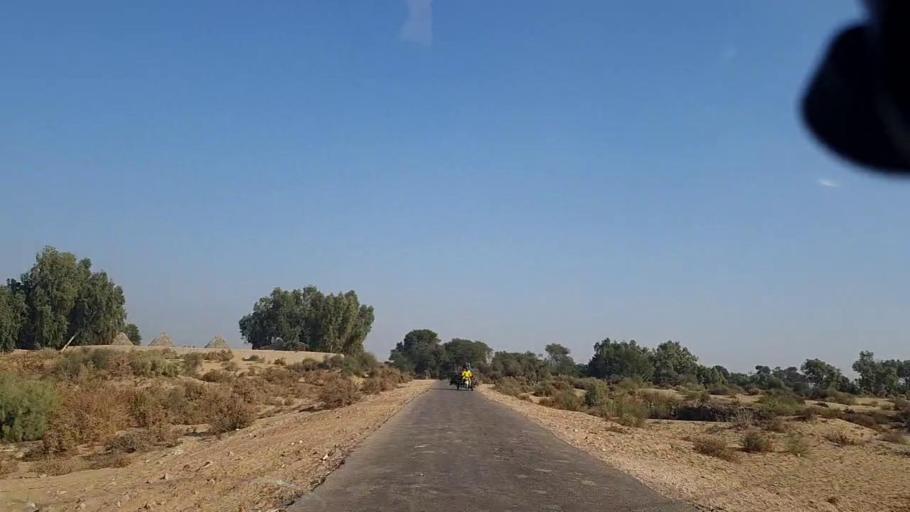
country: PK
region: Sindh
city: Khanpur
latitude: 27.6860
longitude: 69.4848
